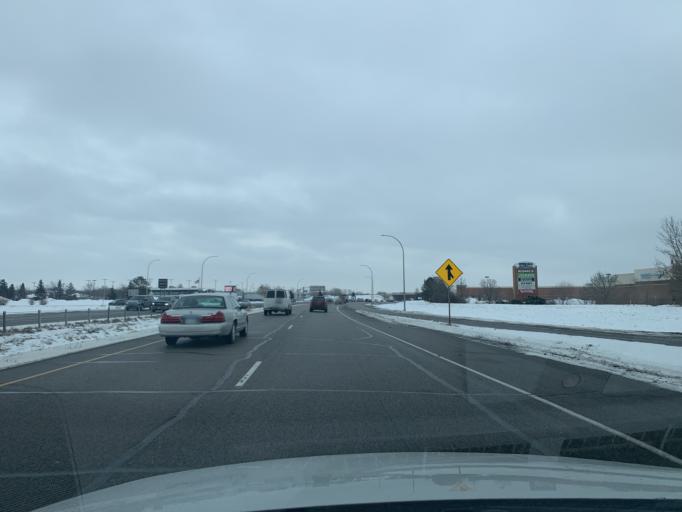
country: US
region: Minnesota
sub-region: Anoka County
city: Anoka
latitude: 45.2042
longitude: -93.3553
